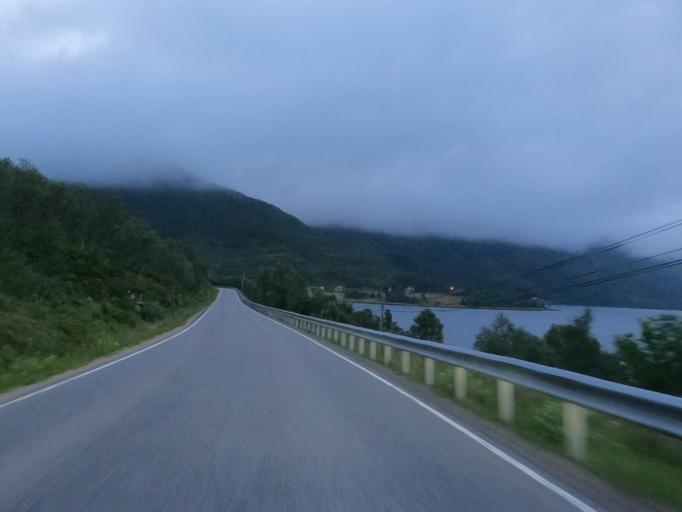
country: NO
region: Nordland
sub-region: Lodingen
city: Lodingen
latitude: 68.6107
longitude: 15.7769
